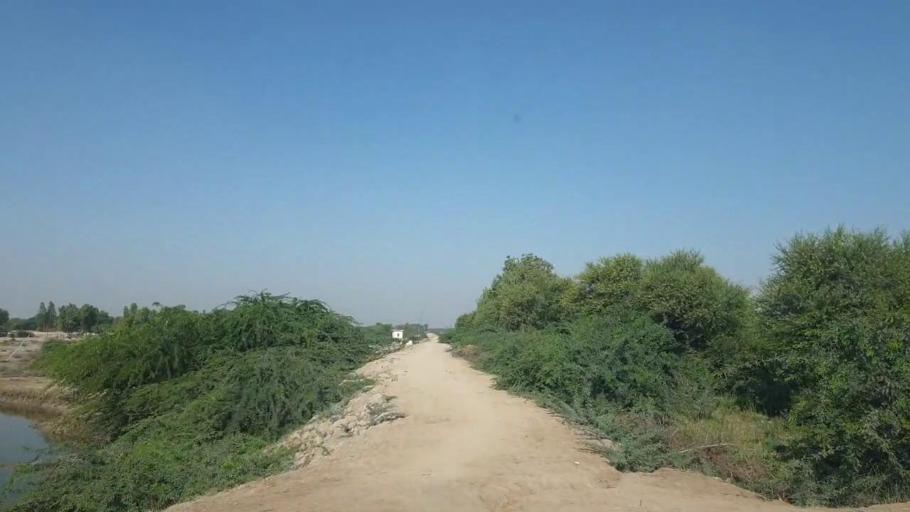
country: PK
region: Sindh
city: Talhar
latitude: 24.7917
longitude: 68.8036
